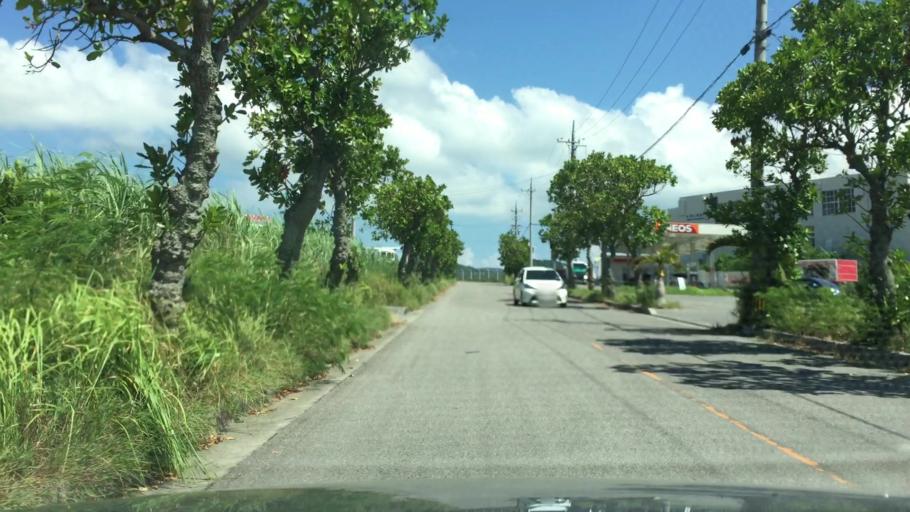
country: JP
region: Okinawa
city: Ishigaki
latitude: 24.3879
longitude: 124.2436
